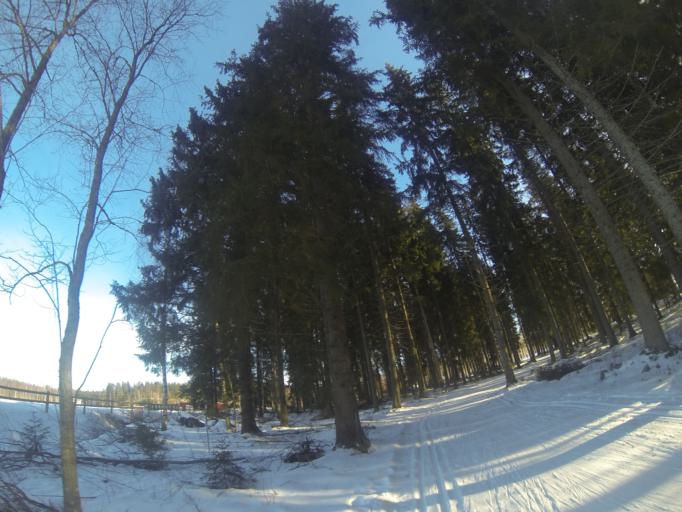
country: FI
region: Southern Savonia
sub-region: Savonlinna
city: Savonlinna
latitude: 61.9176
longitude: 28.9049
